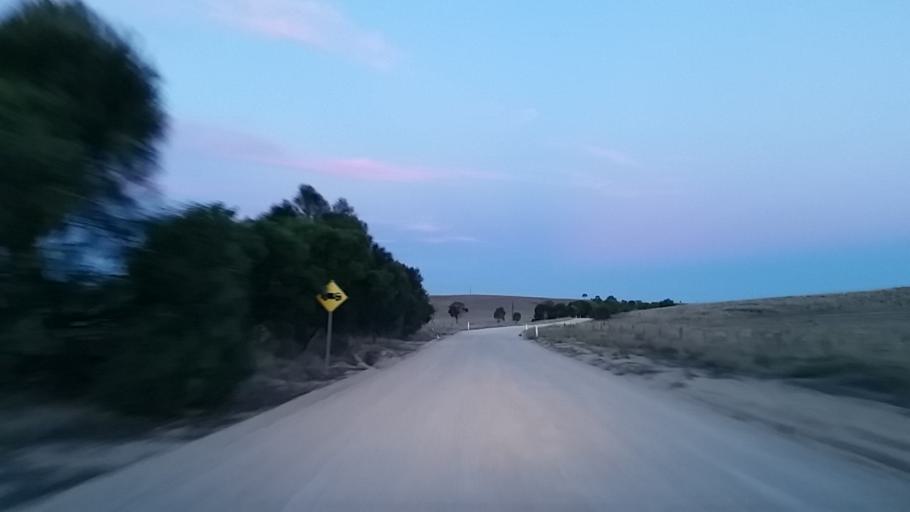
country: AU
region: South Australia
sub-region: Mount Barker
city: Callington
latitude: -35.1054
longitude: 139.0161
